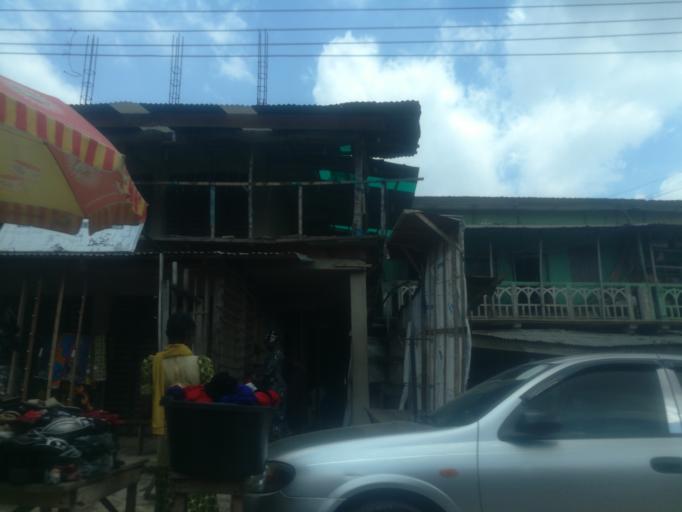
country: NG
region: Oyo
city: Ibadan
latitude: 7.3855
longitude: 3.8846
